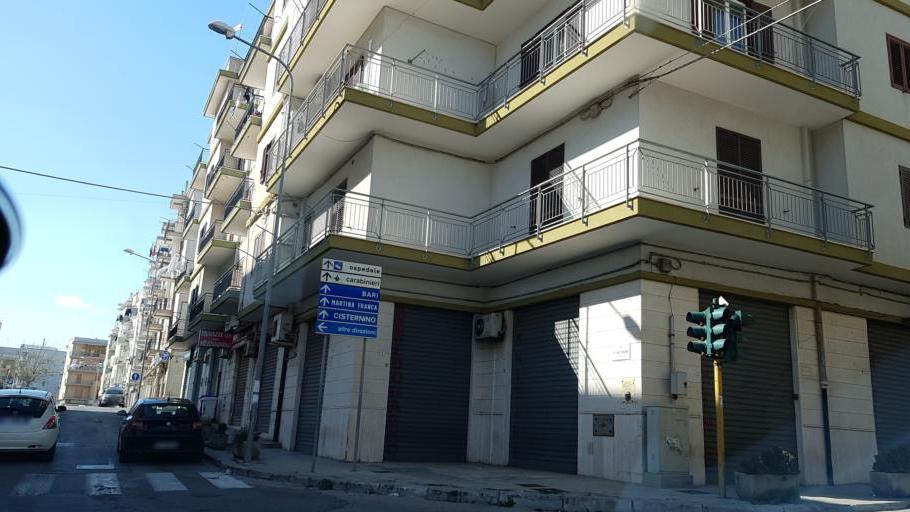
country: IT
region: Apulia
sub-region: Provincia di Brindisi
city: Ostuni
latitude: 40.7234
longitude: 17.5779
